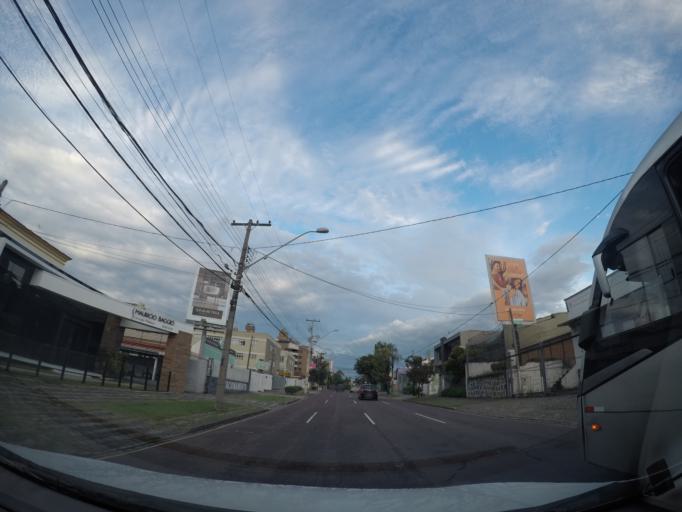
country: BR
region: Parana
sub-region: Curitiba
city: Curitiba
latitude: -25.4268
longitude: -49.2874
